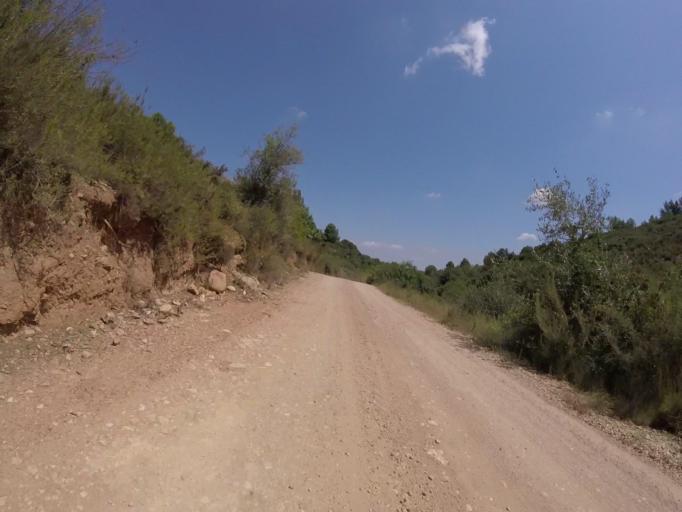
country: ES
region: Valencia
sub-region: Provincia de Castello
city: Torreblanca
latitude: 40.2282
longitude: 0.1574
